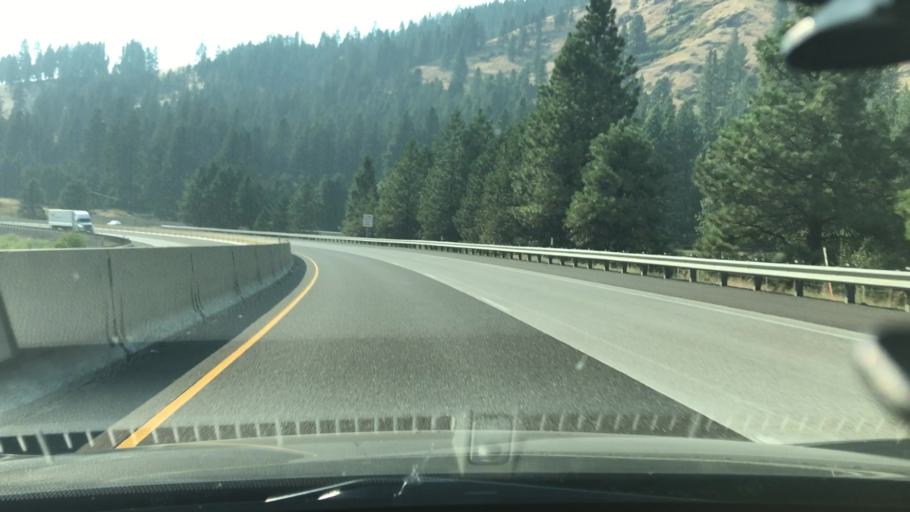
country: US
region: Oregon
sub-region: Union County
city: La Grande
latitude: 45.3545
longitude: -118.1866
